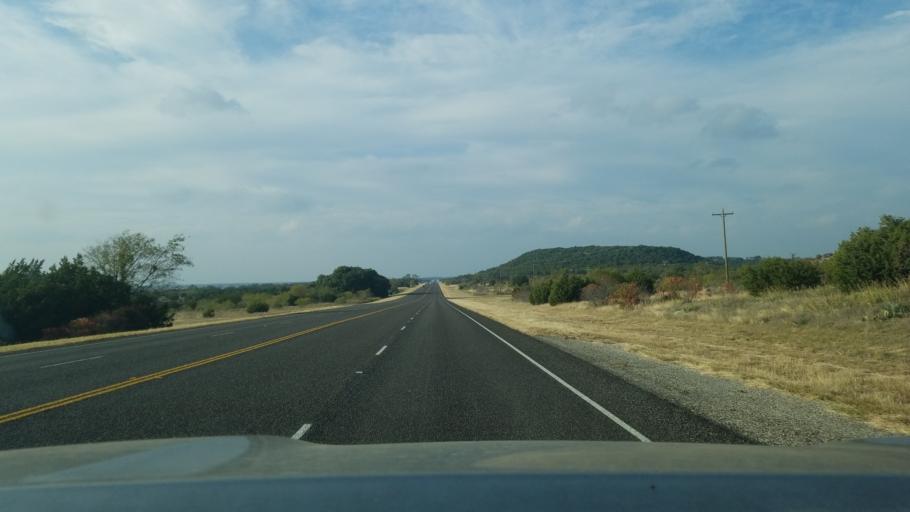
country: US
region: Texas
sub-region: Mills County
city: Goldthwaite
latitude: 31.2617
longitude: -98.4384
